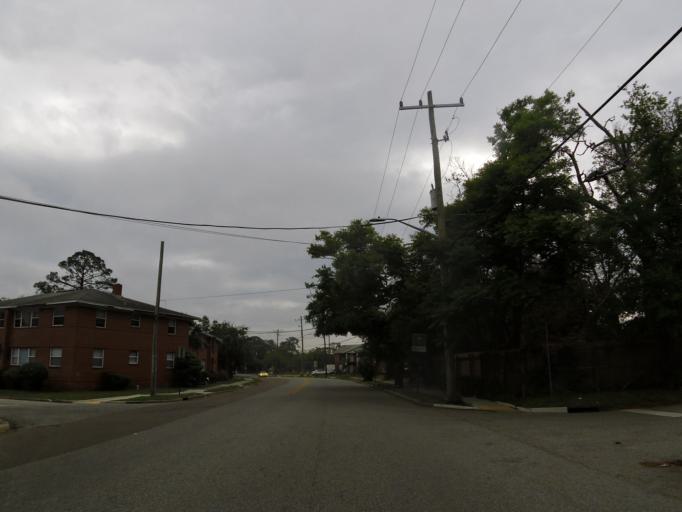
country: US
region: Florida
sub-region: Duval County
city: Jacksonville
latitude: 30.3036
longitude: -81.6352
